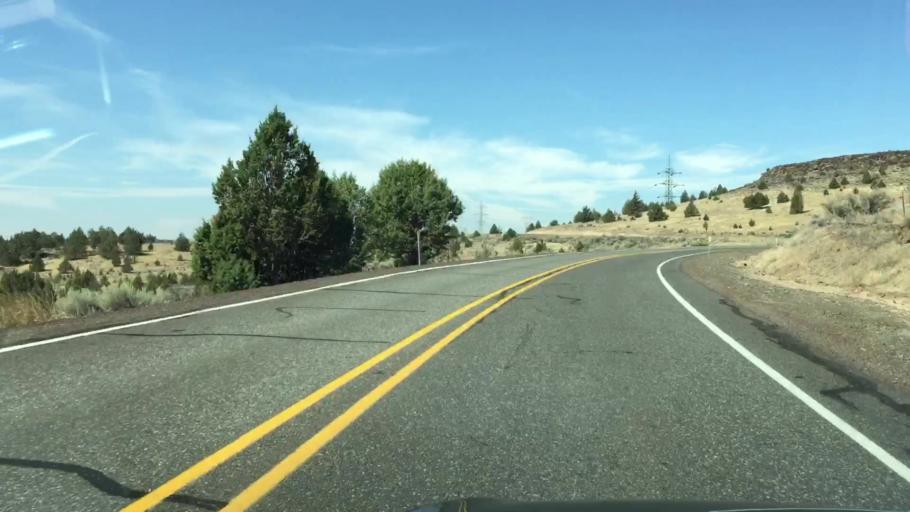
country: US
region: Oregon
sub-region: Wasco County
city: The Dalles
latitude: 45.1691
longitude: -121.0972
